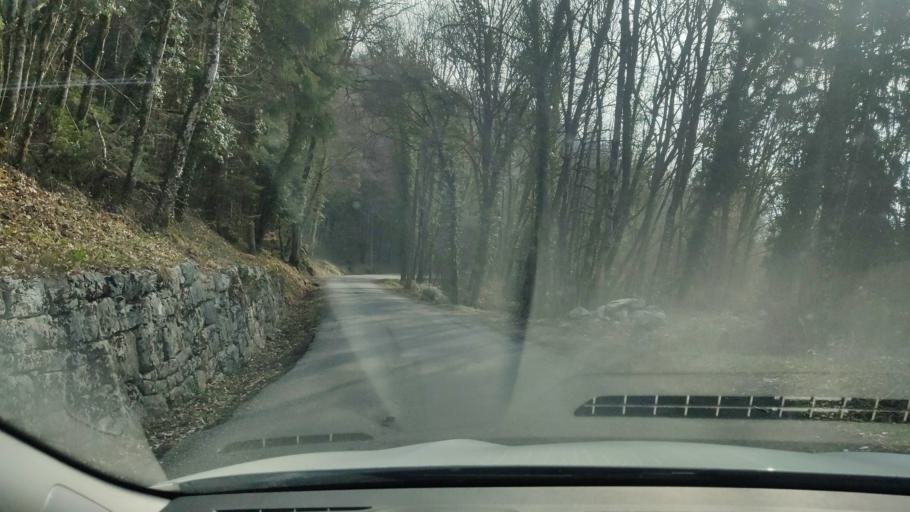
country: FR
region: Rhone-Alpes
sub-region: Departement de la Haute-Savoie
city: Bonneville
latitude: 46.0931
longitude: 6.4117
